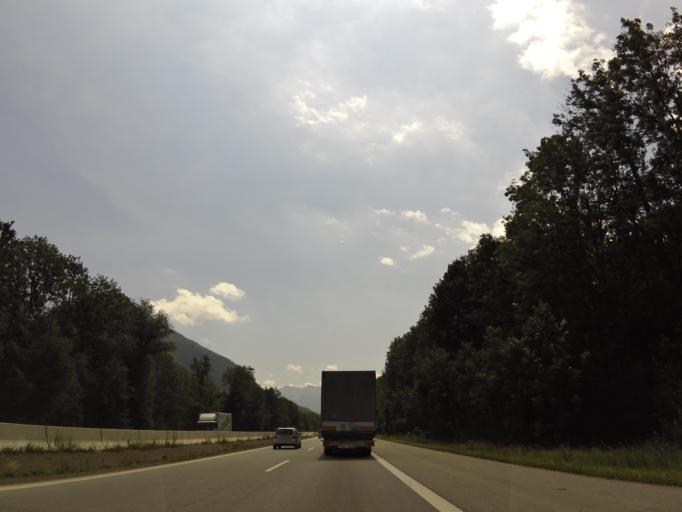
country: DE
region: Bavaria
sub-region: Upper Bavaria
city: Flintsbach
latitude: 47.7157
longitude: 12.1464
